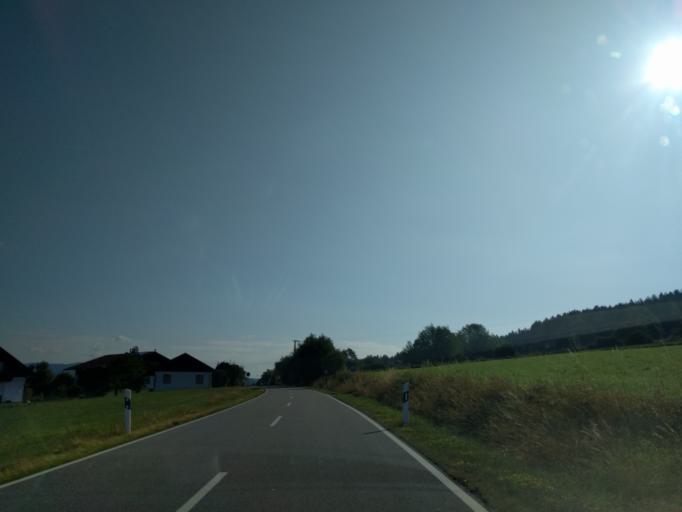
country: DE
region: Bavaria
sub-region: Lower Bavaria
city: Neuschonau
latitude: 48.8538
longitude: 13.4442
